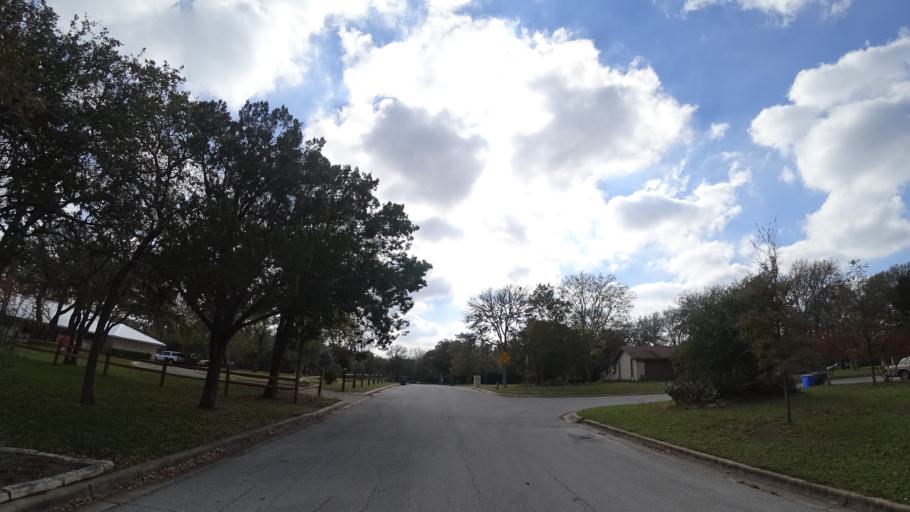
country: US
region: Texas
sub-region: Travis County
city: Shady Hollow
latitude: 30.1683
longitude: -97.8549
